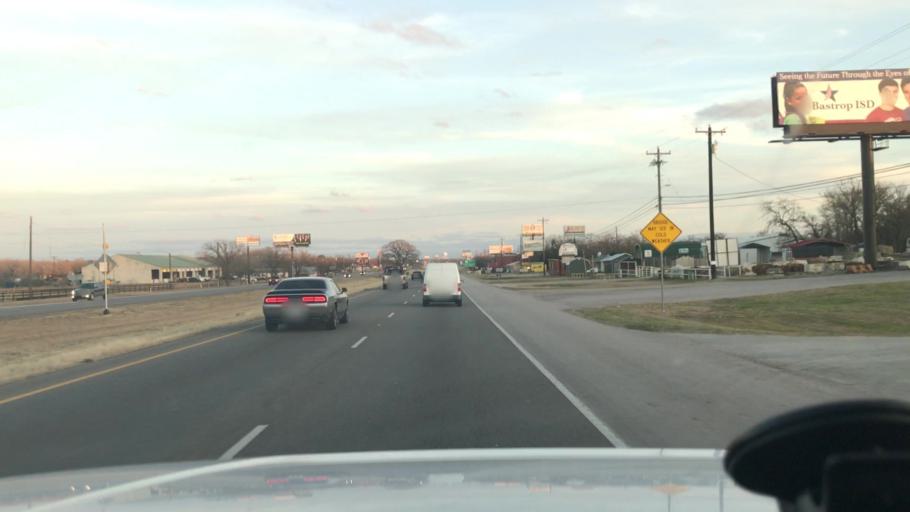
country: US
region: Texas
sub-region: Bastrop County
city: Wyldwood
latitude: 30.1196
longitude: -97.4283
